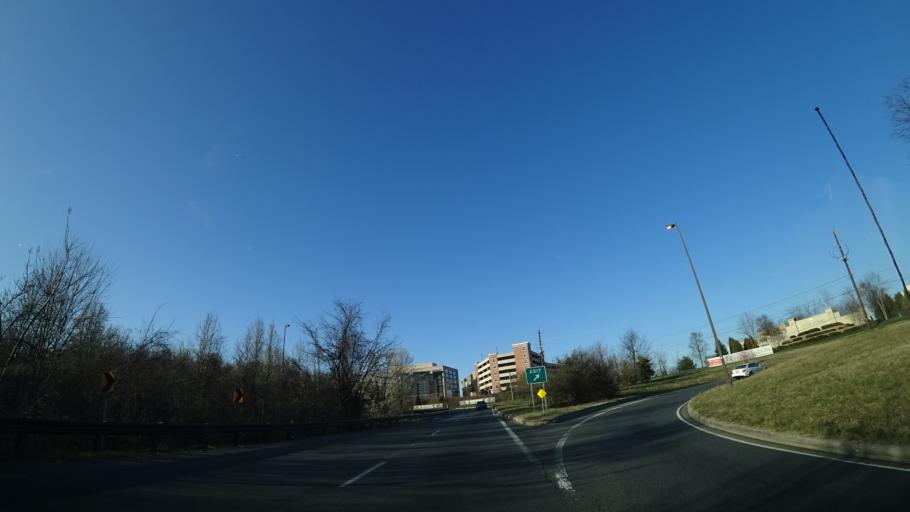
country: US
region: Maryland
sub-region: Montgomery County
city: Derwood
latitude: 39.1096
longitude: -77.1854
